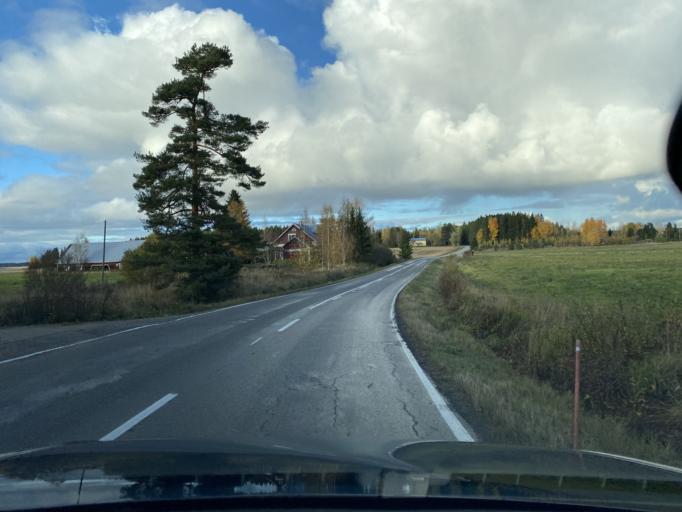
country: FI
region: Haeme
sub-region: Forssa
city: Humppila
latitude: 61.0199
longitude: 23.2479
